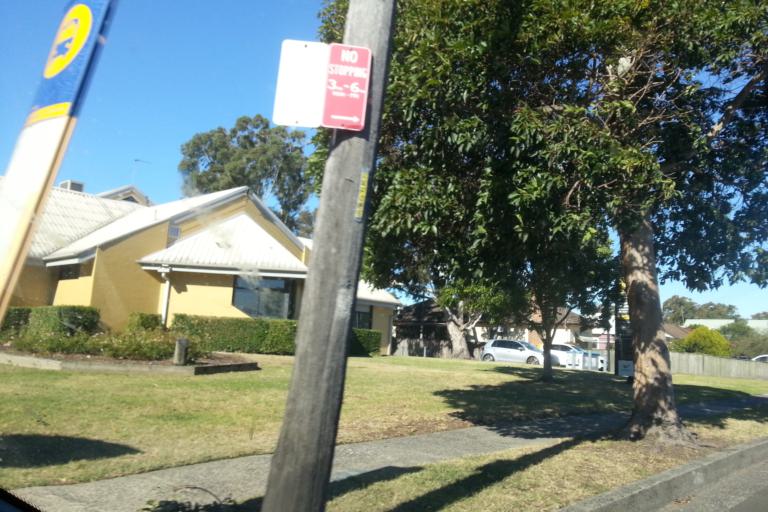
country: AU
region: New South Wales
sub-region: Wollongong
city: Dapto
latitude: -34.4968
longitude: 150.7924
